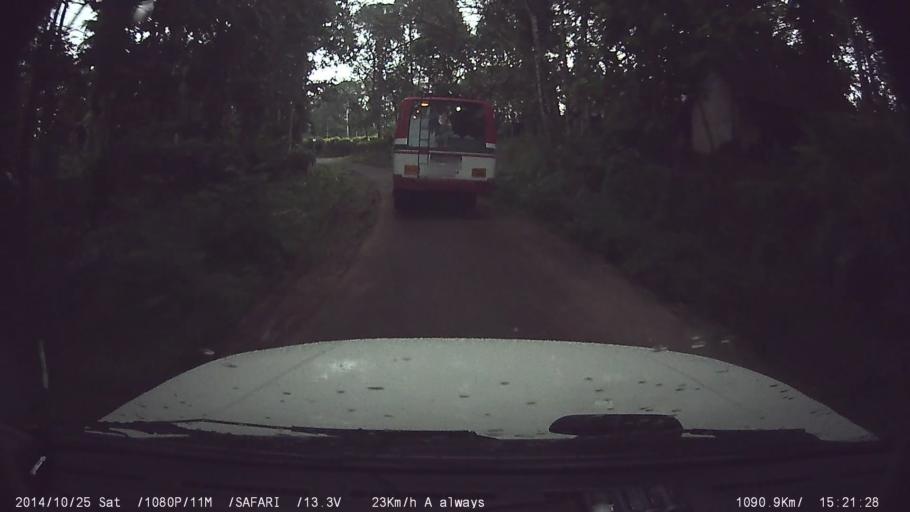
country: IN
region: Kerala
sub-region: Kottayam
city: Palackattumala
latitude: 9.7824
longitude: 76.5699
